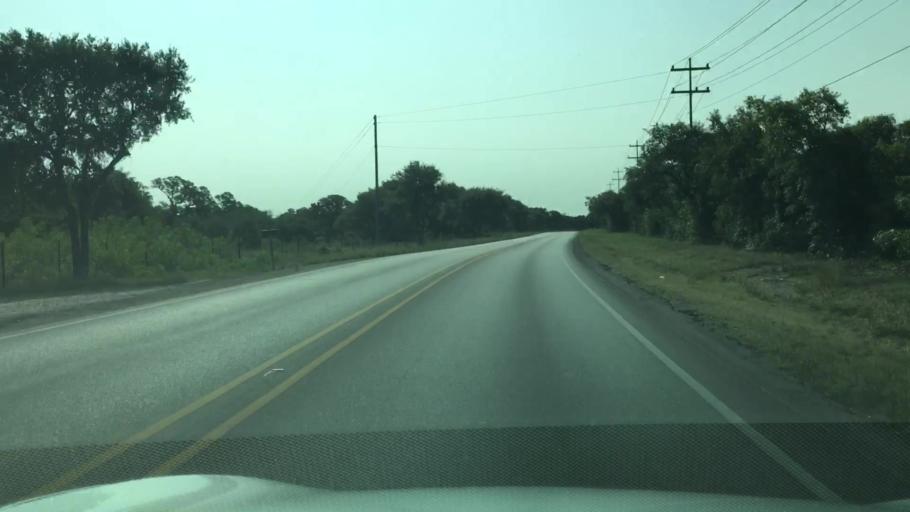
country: US
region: Texas
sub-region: Travis County
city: Shady Hollow
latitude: 30.1167
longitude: -97.9559
